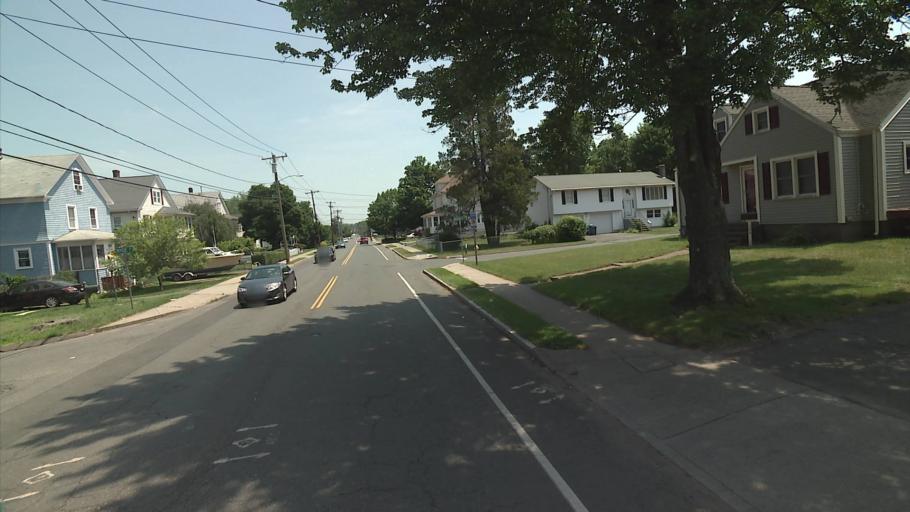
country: US
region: Connecticut
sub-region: Hartford County
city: Manchester
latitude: 41.7705
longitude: -72.5467
